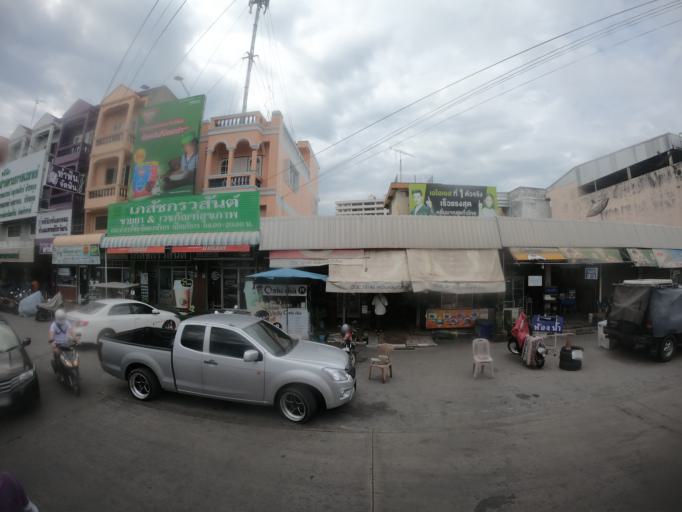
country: TH
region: Maha Sarakham
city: Maha Sarakham
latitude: 16.1811
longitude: 103.3012
